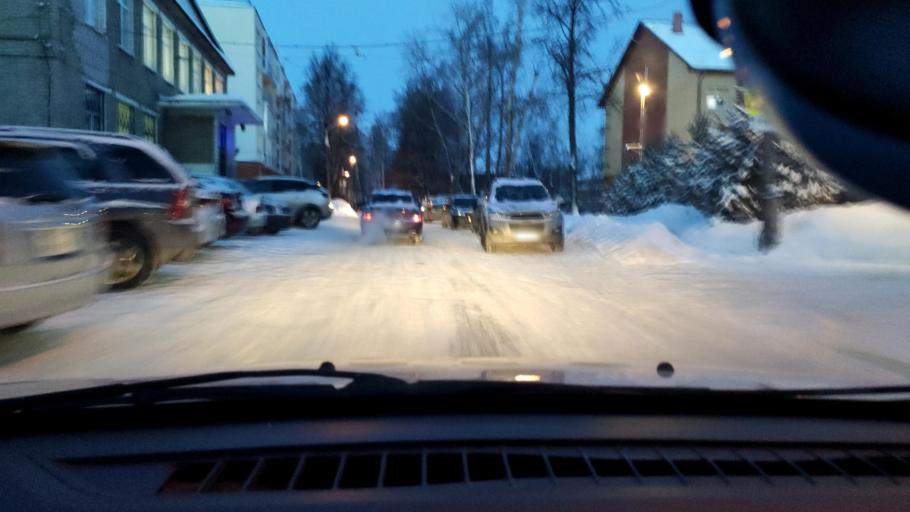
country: RU
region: Perm
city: Kondratovo
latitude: 58.0223
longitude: 56.0171
